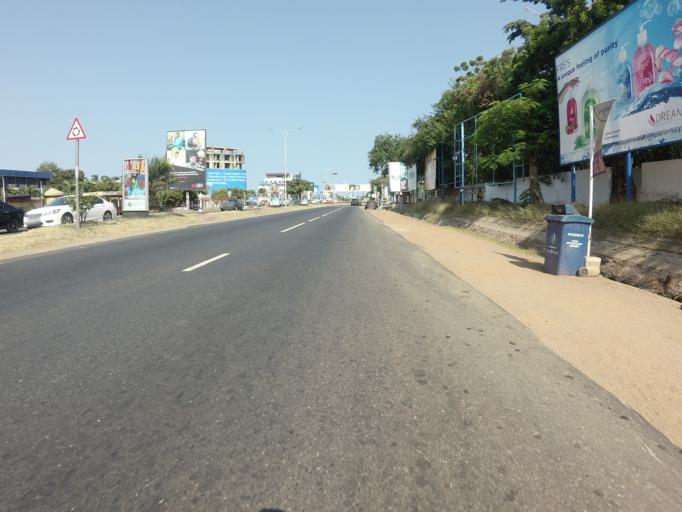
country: GH
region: Greater Accra
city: Accra
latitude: 5.5675
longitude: -0.1821
